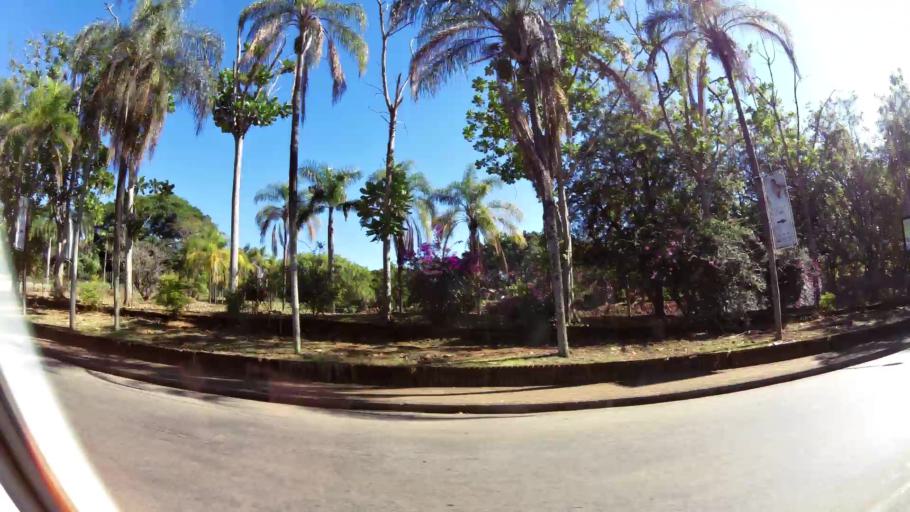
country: ZA
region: Limpopo
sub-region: Mopani District Municipality
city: Tzaneen
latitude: -23.8401
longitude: 30.1514
